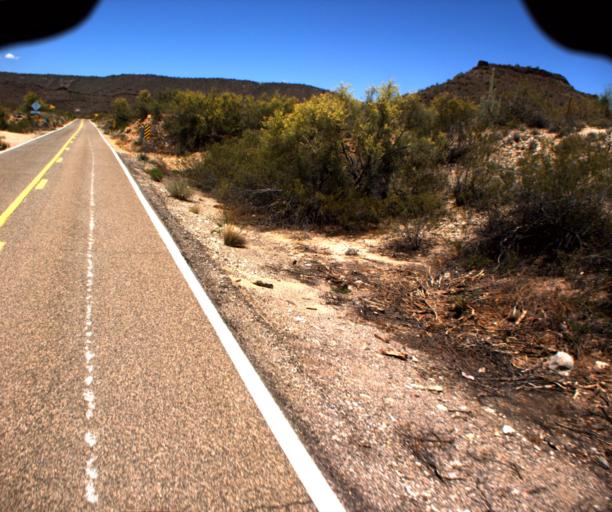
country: US
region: Arizona
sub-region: Yavapai County
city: Bagdad
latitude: 34.4861
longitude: -113.0645
